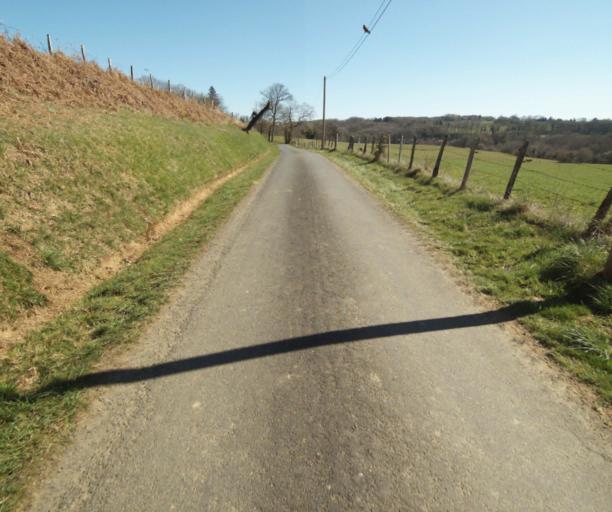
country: FR
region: Limousin
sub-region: Departement de la Correze
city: Chamboulive
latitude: 45.3960
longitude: 1.6547
